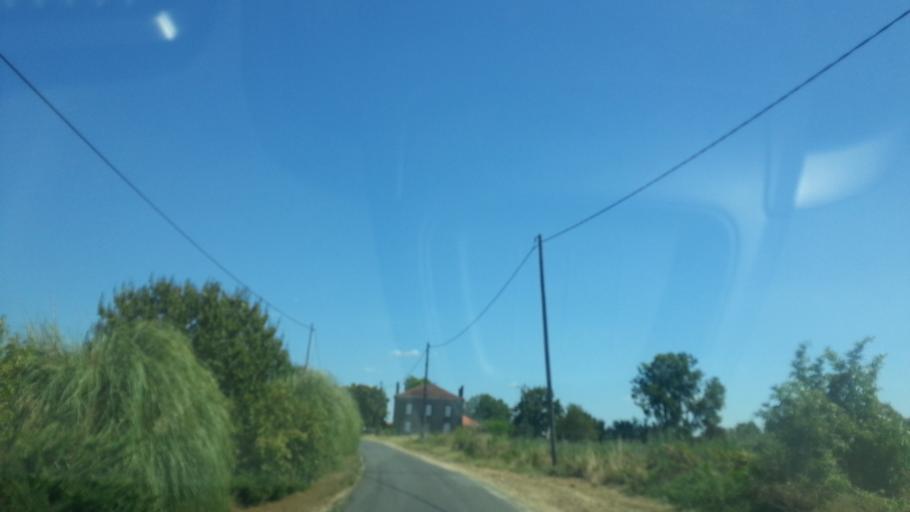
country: FR
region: Aquitaine
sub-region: Departement de la Gironde
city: Landiras
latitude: 44.5794
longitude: -0.3972
